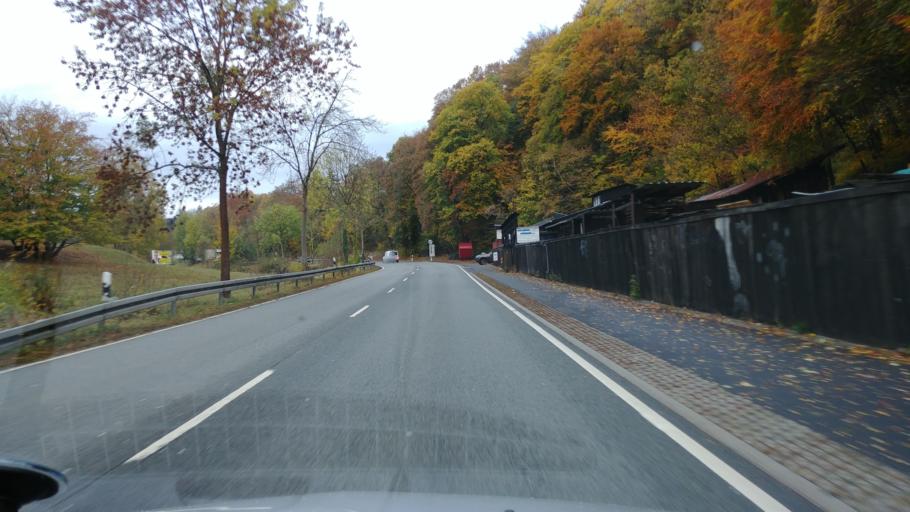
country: DE
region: Hesse
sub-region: Regierungsbezirk Darmstadt
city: Schlangenbad
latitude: 50.1049
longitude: 8.1022
